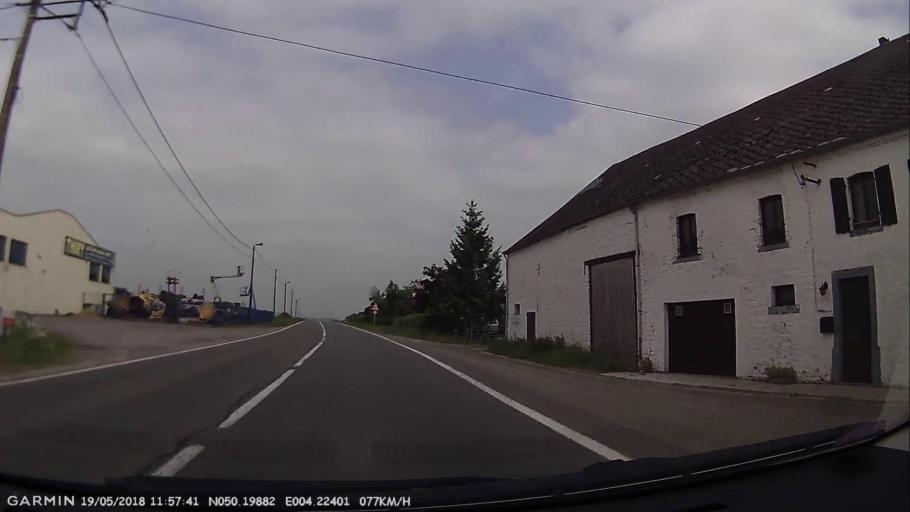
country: BE
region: Wallonia
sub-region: Province du Hainaut
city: Beaumont
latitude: 50.1990
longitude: 4.2241
